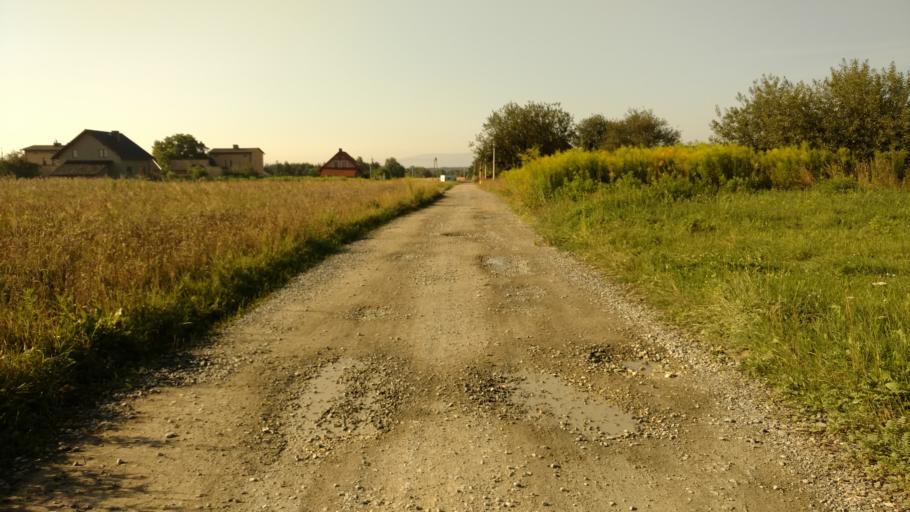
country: PL
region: Silesian Voivodeship
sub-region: Powiat pszczynski
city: Pszczyna
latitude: 49.9911
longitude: 18.9674
